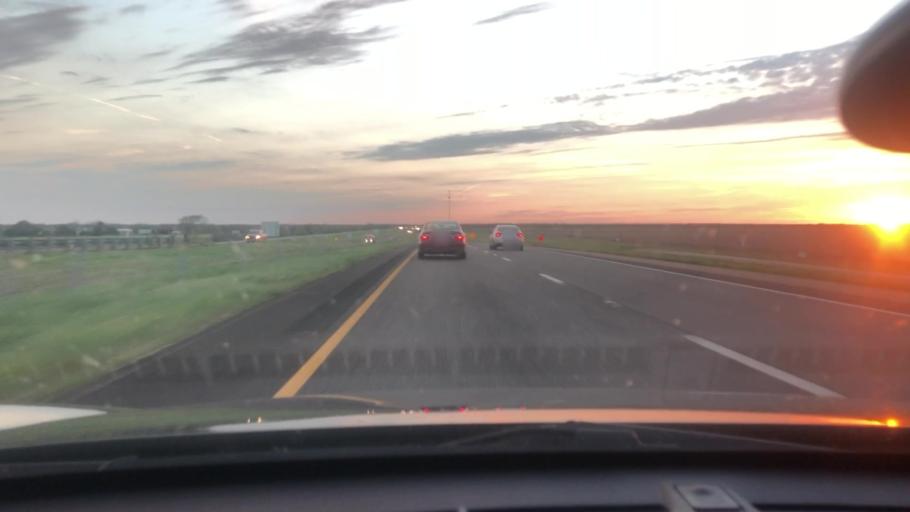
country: US
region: Texas
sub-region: Victoria County
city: Inez
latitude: 28.9340
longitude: -96.7354
